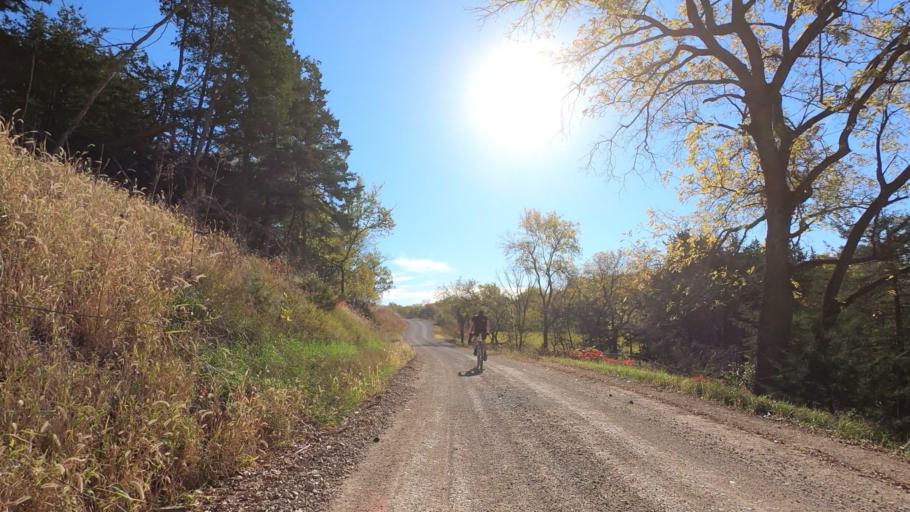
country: US
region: Kansas
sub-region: Pottawatomie County
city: Westmoreland
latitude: 39.4824
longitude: -96.5957
